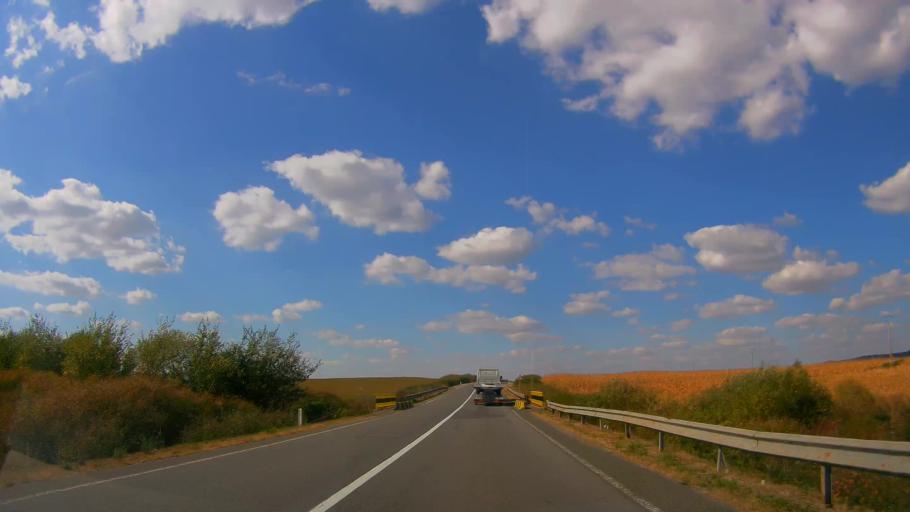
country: RO
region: Salaj
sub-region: Comuna Bobota
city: Dersida
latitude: 47.3605
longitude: 22.7960
